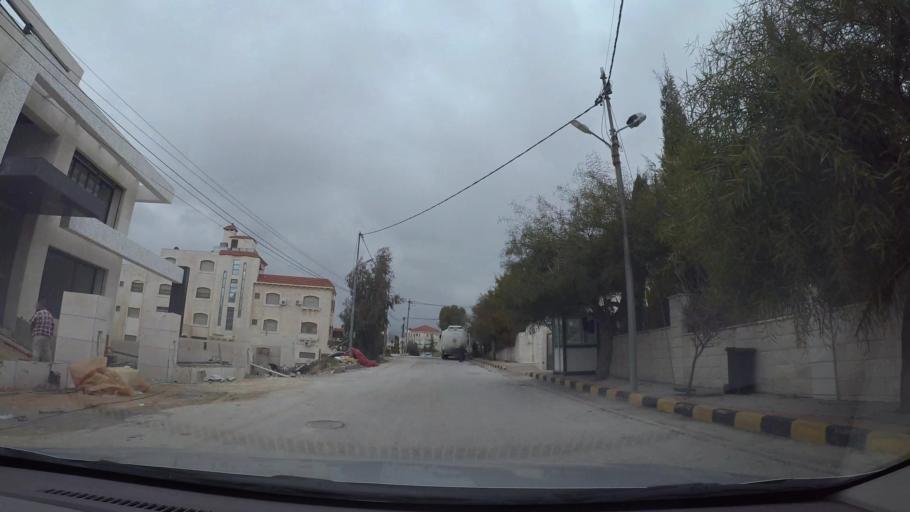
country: JO
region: Amman
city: Wadi as Sir
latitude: 31.9925
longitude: 35.8340
